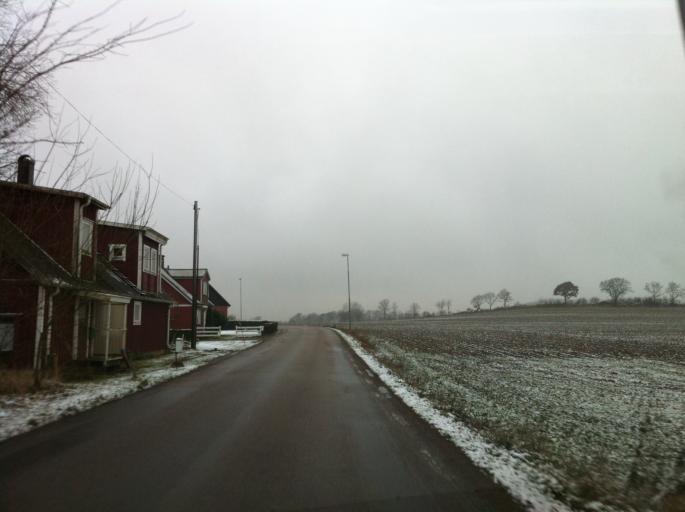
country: SE
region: Skane
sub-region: Bjuvs Kommun
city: Billesholm
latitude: 55.9859
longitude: 13.0003
